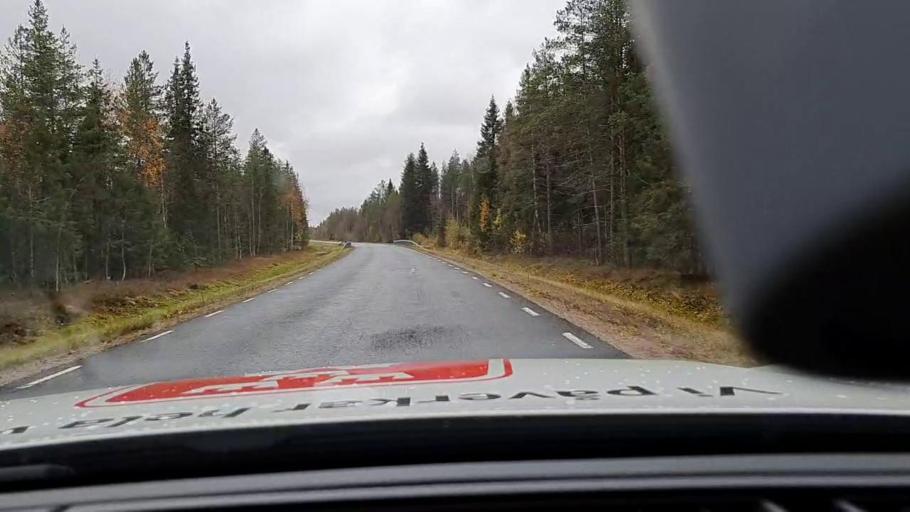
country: SE
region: Norrbotten
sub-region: Haparanda Kommun
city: Haparanda
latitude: 65.9037
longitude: 23.8335
